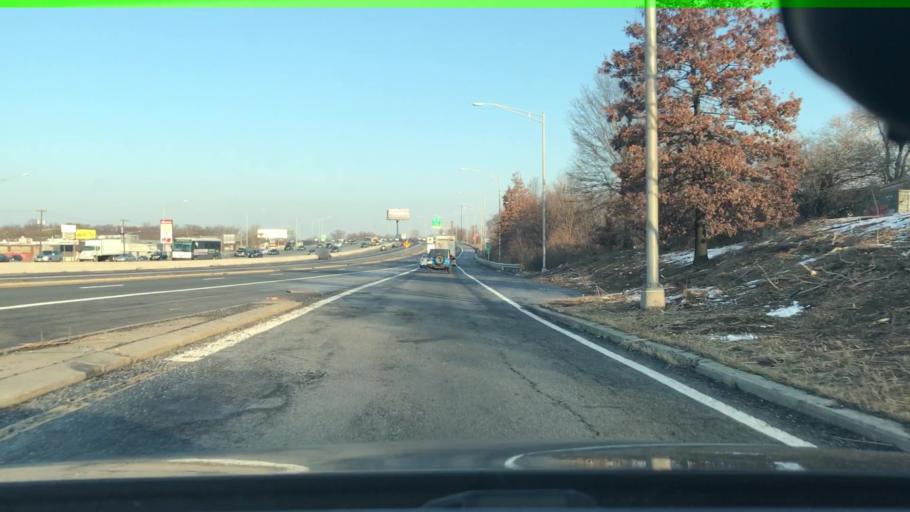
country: US
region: New Jersey
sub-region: Bergen County
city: Lodi
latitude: 40.8812
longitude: -74.0651
